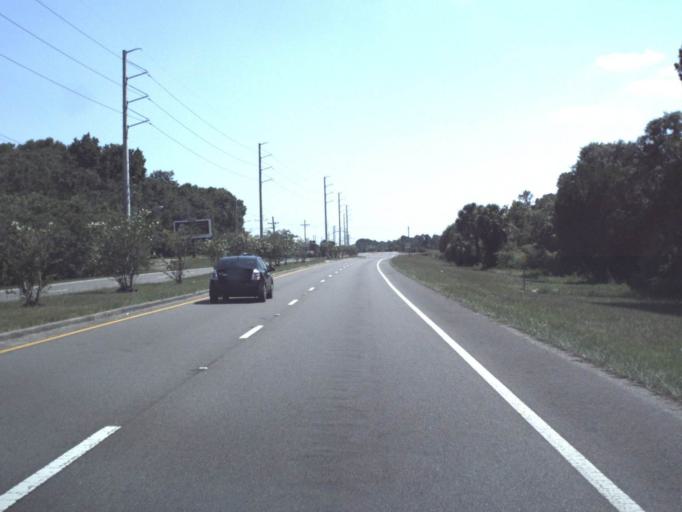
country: US
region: Florida
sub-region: Duval County
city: Jacksonville
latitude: 30.4279
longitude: -81.6457
